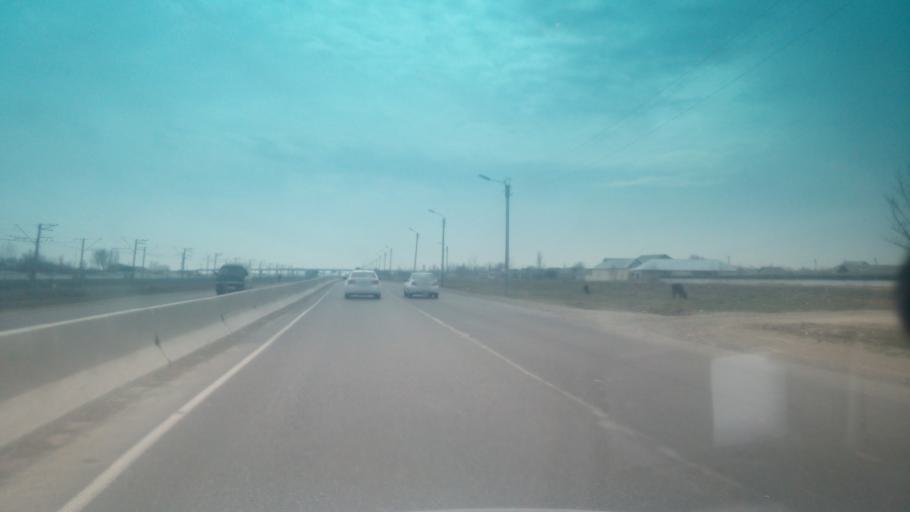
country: UZ
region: Sirdaryo
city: Guliston
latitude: 40.4828
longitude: 68.7681
